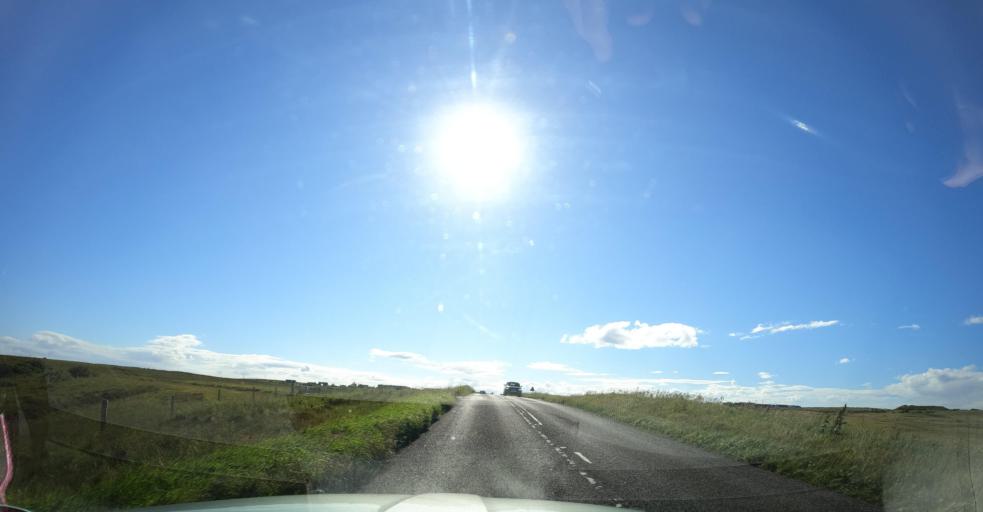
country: GB
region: Scotland
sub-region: Eilean Siar
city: Stornoway
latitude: 58.2034
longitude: -6.3290
